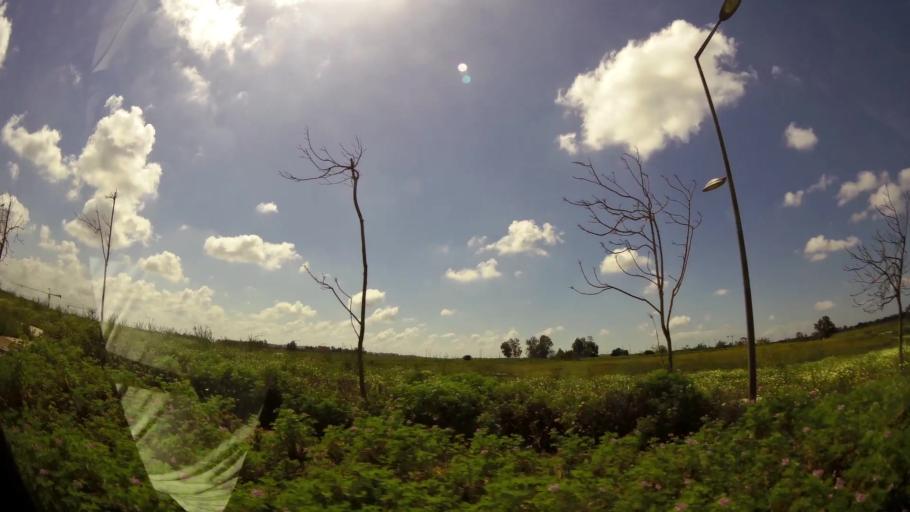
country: MA
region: Grand Casablanca
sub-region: Nouaceur
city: Bouskoura
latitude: 33.4945
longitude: -7.6035
